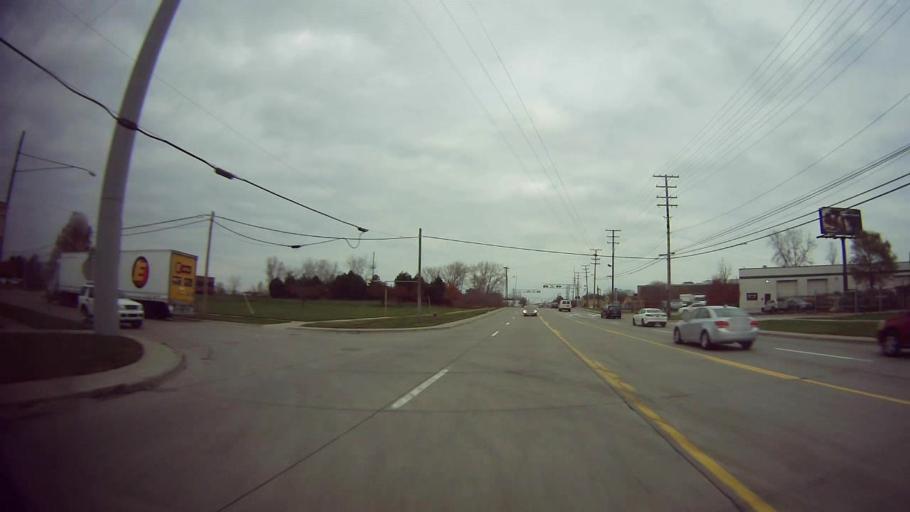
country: US
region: Michigan
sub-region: Macomb County
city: Warren
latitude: 42.4638
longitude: -82.9962
